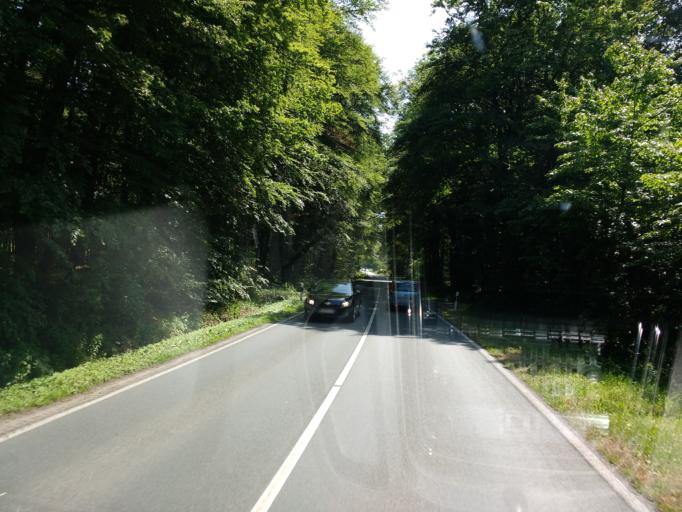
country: DE
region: Lower Saxony
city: Belm
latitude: 52.3226
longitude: 8.1121
